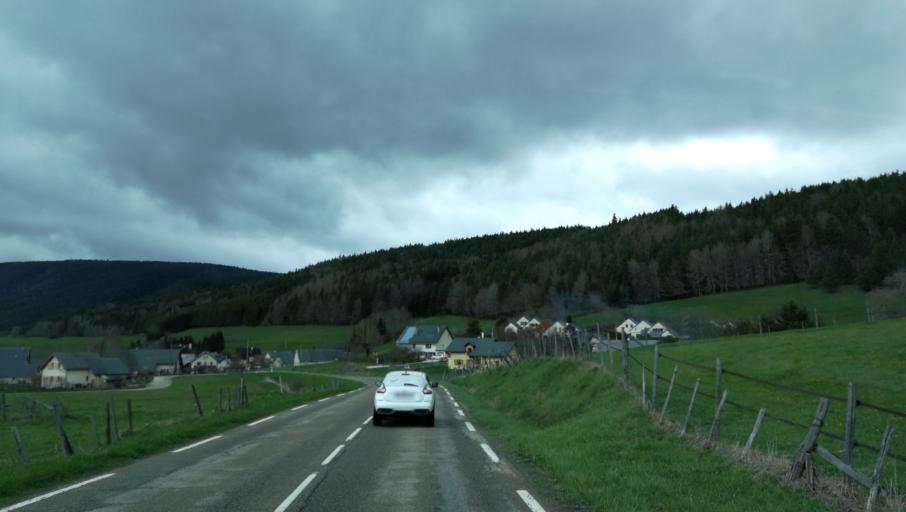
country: FR
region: Rhone-Alpes
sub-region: Departement de l'Isere
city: Lans-en-Vercors
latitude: 45.1132
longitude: 5.5717
